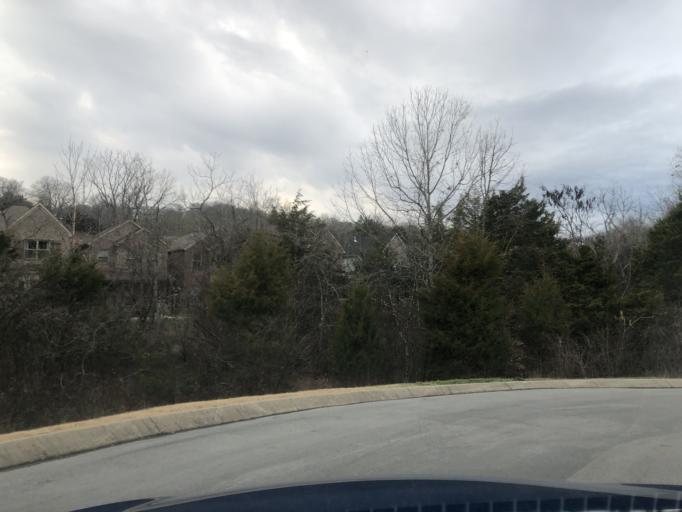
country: US
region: Tennessee
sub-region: Davidson County
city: Belle Meade
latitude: 36.1024
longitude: -86.9312
